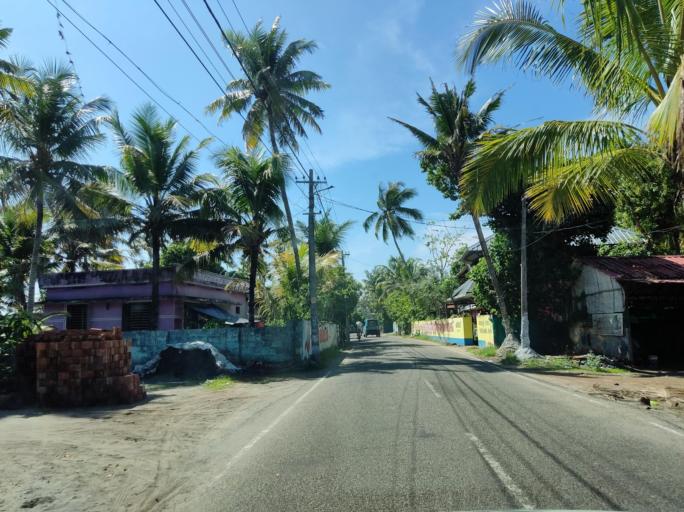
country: IN
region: Kerala
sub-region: Alappuzha
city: Kayankulam
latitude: 9.2270
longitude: 76.4222
